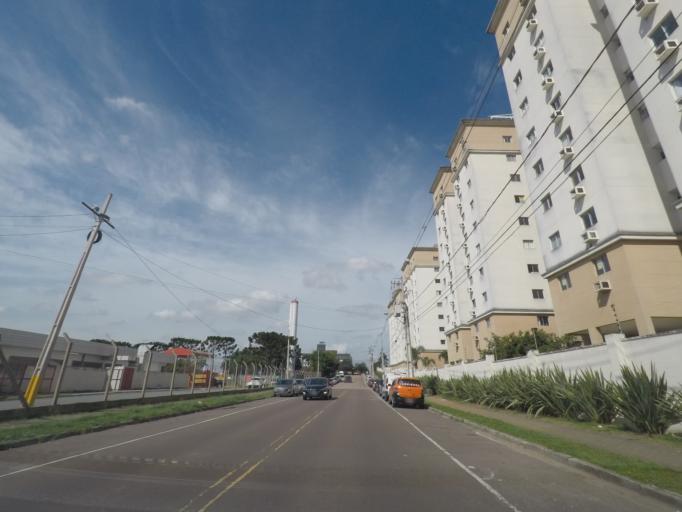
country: BR
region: Parana
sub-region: Curitiba
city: Curitiba
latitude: -25.4716
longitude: -49.2676
